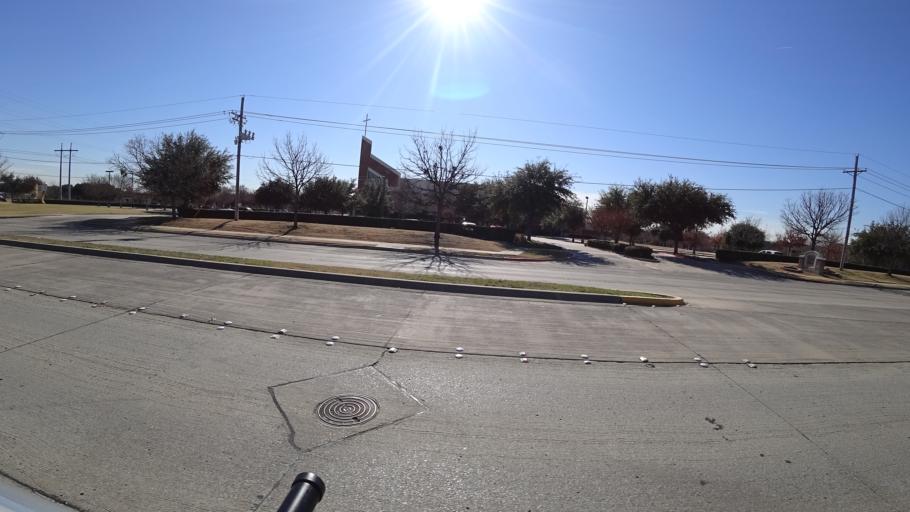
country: US
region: Texas
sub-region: Denton County
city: Lewisville
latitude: 33.0277
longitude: -97.0118
